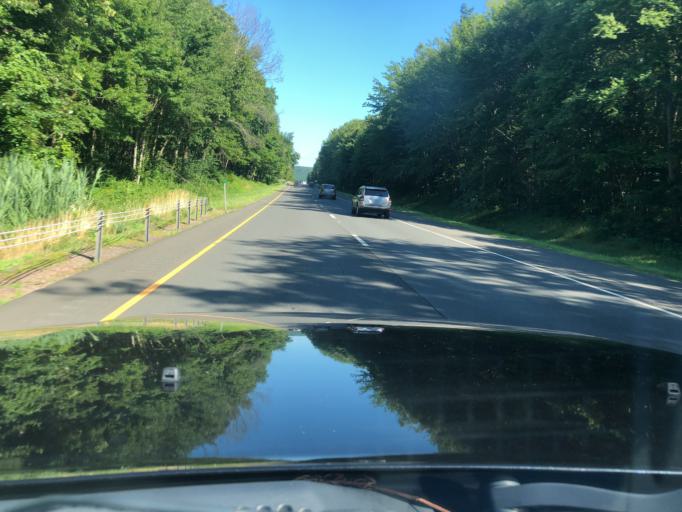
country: US
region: Connecticut
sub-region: Middlesex County
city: Higganum
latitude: 41.5026
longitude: -72.5812
